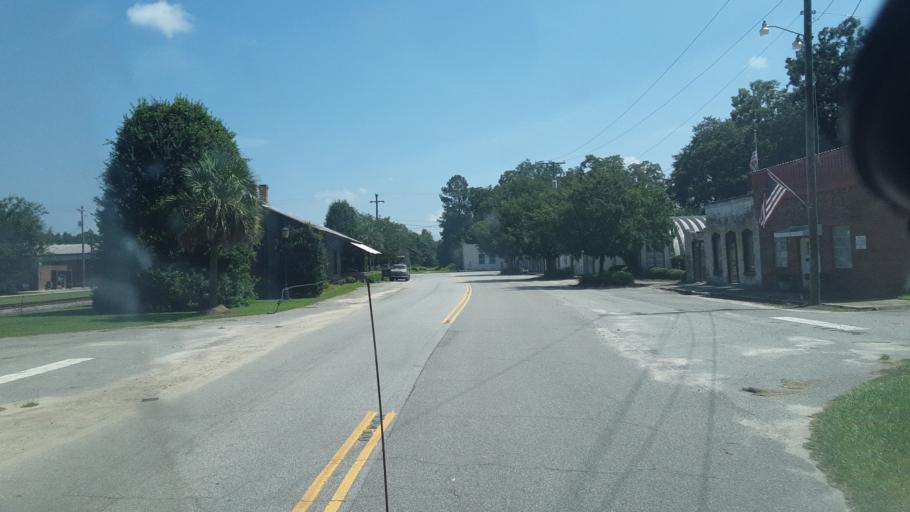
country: US
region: South Carolina
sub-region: Bamberg County
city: Bamberg
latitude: 33.3774
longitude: -81.0083
